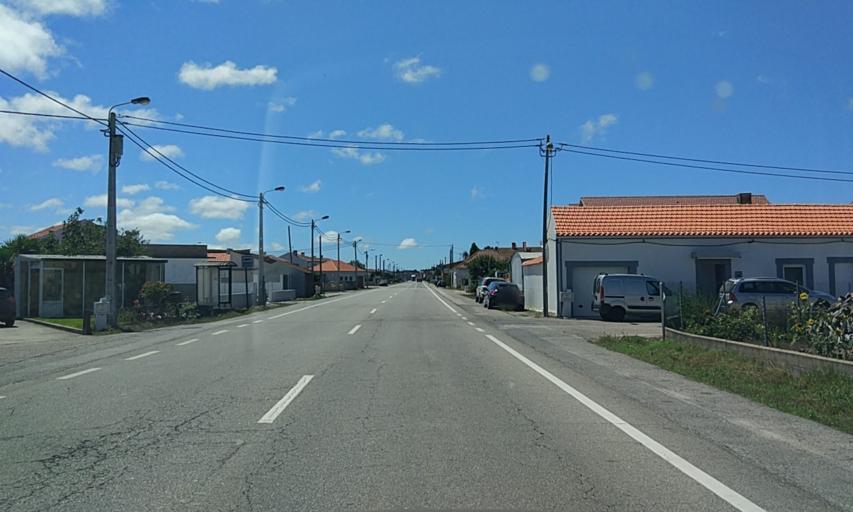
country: PT
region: Aveiro
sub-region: Vagos
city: Vagos
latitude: 40.4848
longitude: -8.6893
